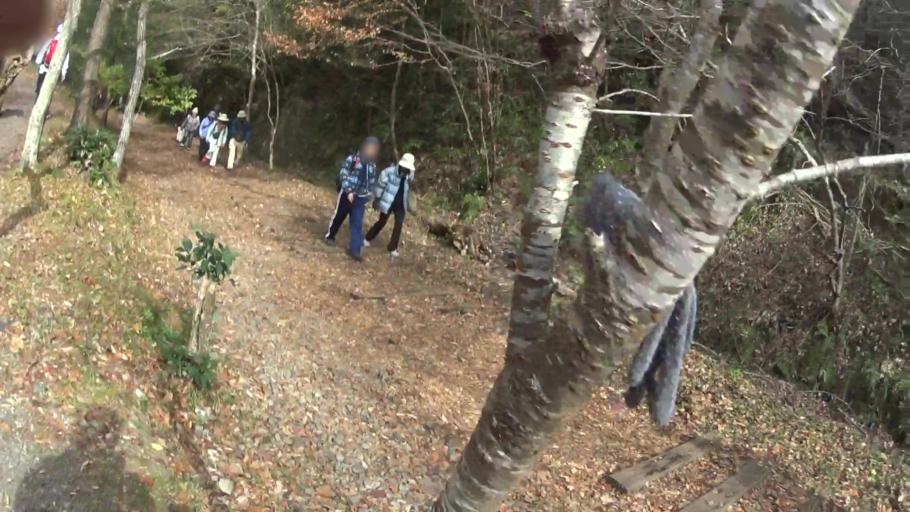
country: JP
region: Hyogo
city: Takarazuka
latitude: 34.8531
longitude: 135.3165
